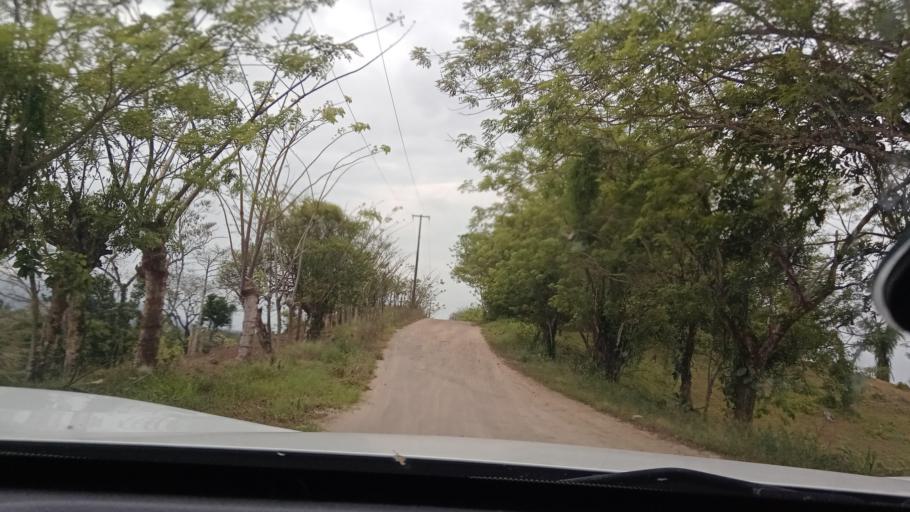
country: MX
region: Tabasco
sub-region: Huimanguillo
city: Francisco Rueda
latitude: 17.5800
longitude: -94.0652
